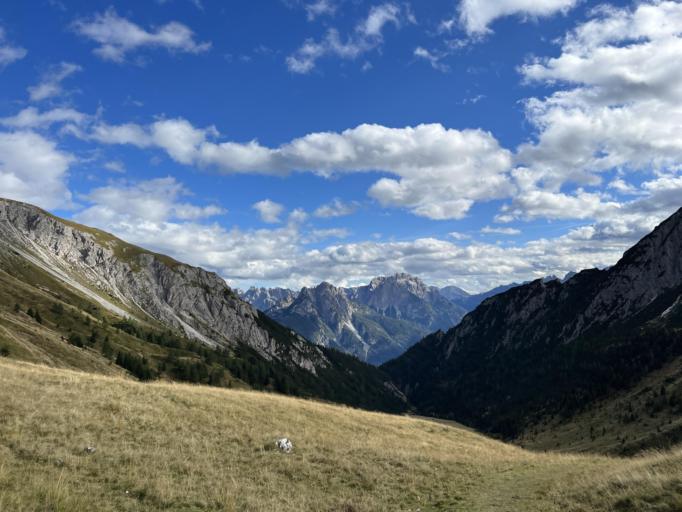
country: IT
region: Veneto
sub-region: Provincia di Belluno
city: San Pietro di Cadore
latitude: 46.6249
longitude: 12.5806
